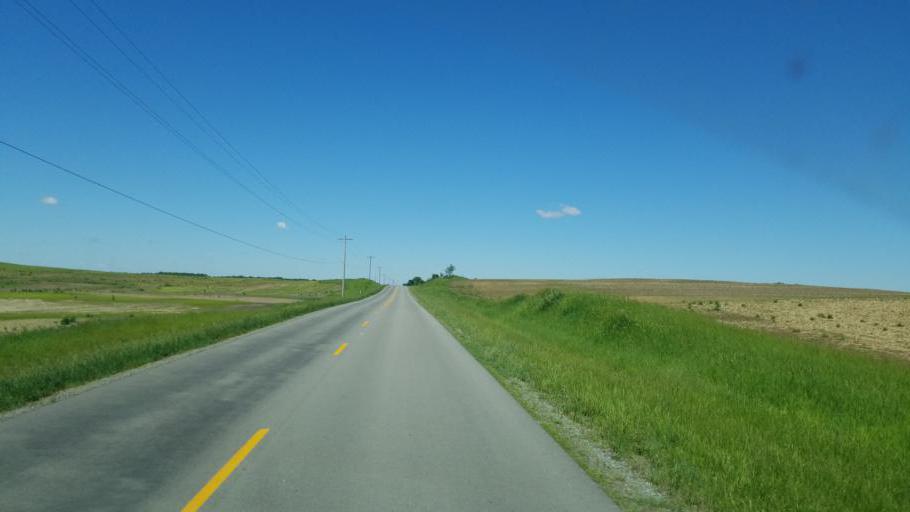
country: US
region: Ohio
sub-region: Logan County
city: Russells Point
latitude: 40.4277
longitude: -83.8184
